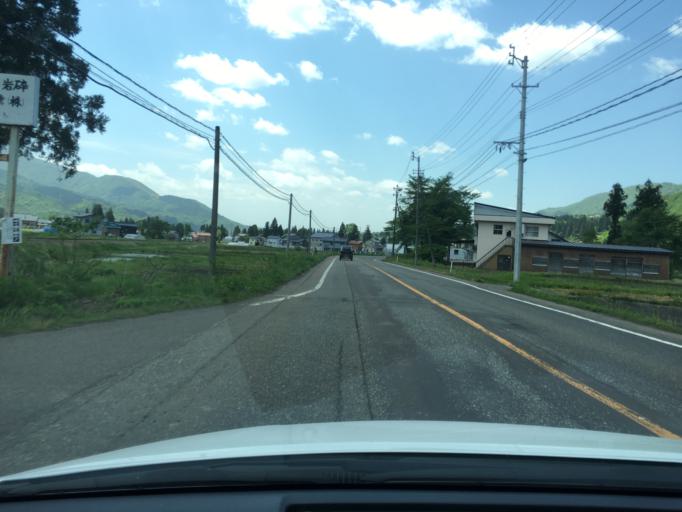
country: JP
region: Niigata
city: Tochio-honcho
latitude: 37.3358
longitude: 139.0344
